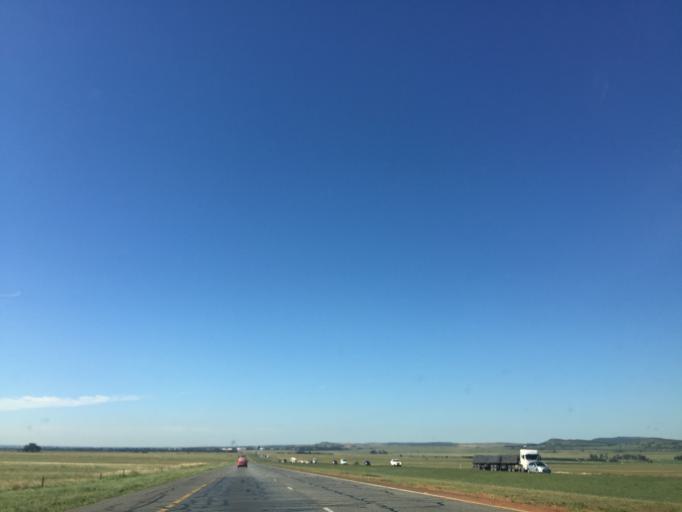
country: ZA
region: Gauteng
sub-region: Ekurhuleni Metropolitan Municipality
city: Germiston
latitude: -26.3636
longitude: 28.0952
